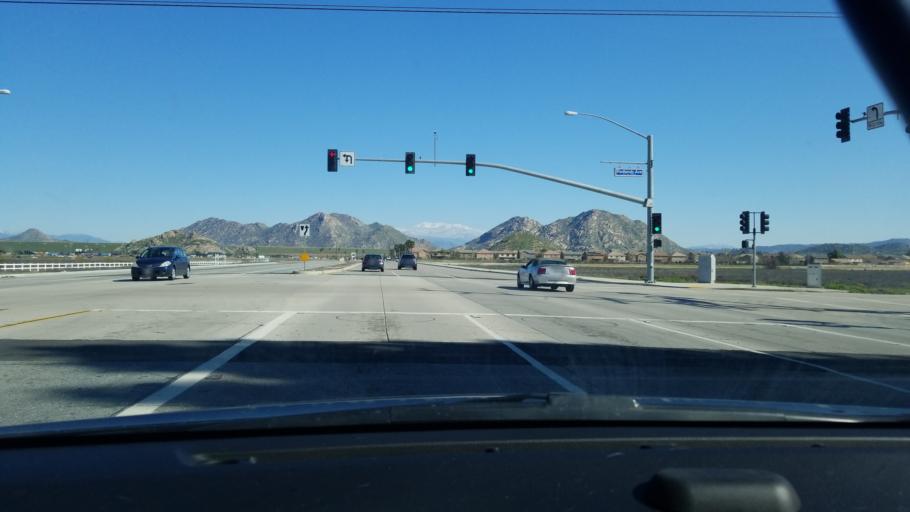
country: US
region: California
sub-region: Riverside County
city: Perris
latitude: 33.8445
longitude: -117.2172
